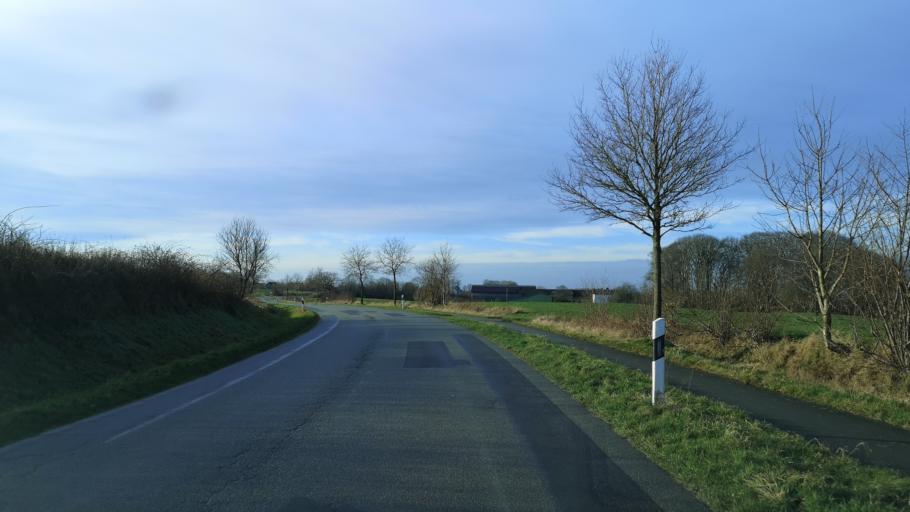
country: DE
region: Schleswig-Holstein
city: Havetoft
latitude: 54.6581
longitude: 9.5280
